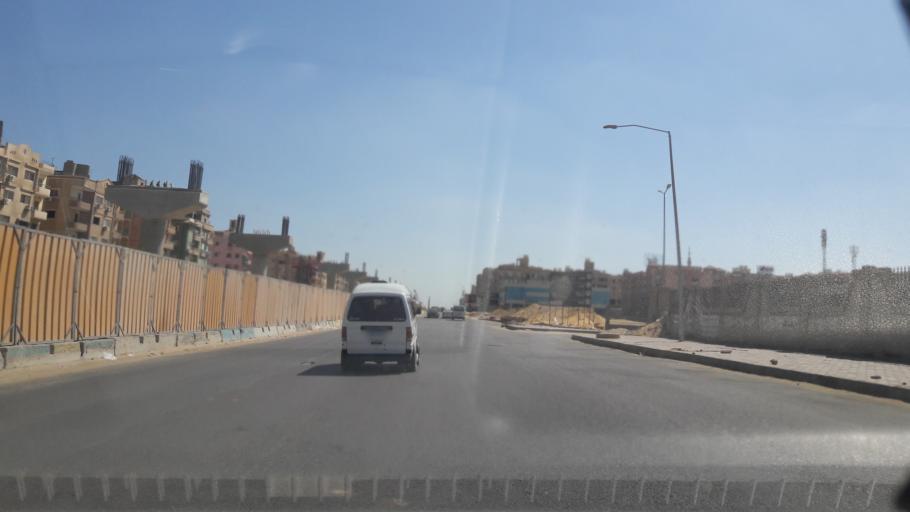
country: EG
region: Al Jizah
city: Madinat Sittah Uktubar
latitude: 29.9717
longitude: 30.9373
